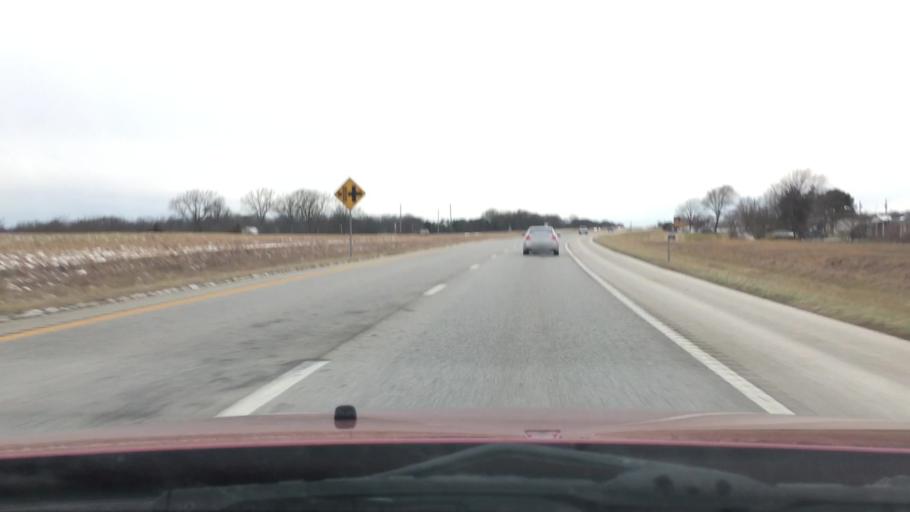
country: US
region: Missouri
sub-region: Webster County
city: Seymour
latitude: 37.1694
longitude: -92.8241
